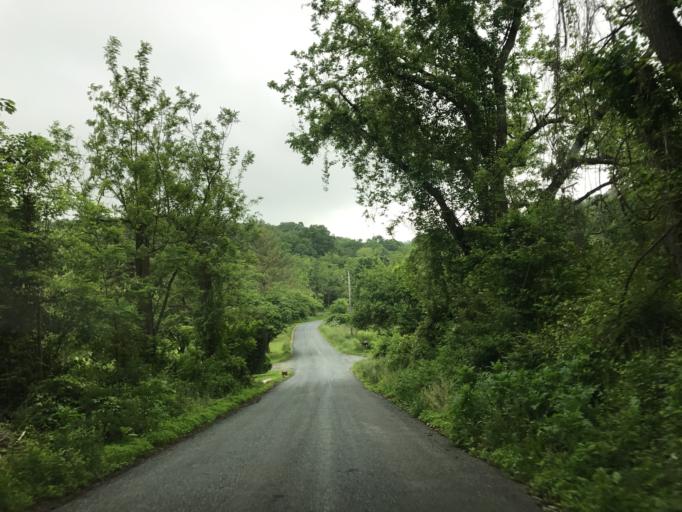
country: US
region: Maryland
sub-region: Harford County
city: Jarrettsville
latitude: 39.7066
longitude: -76.4800
